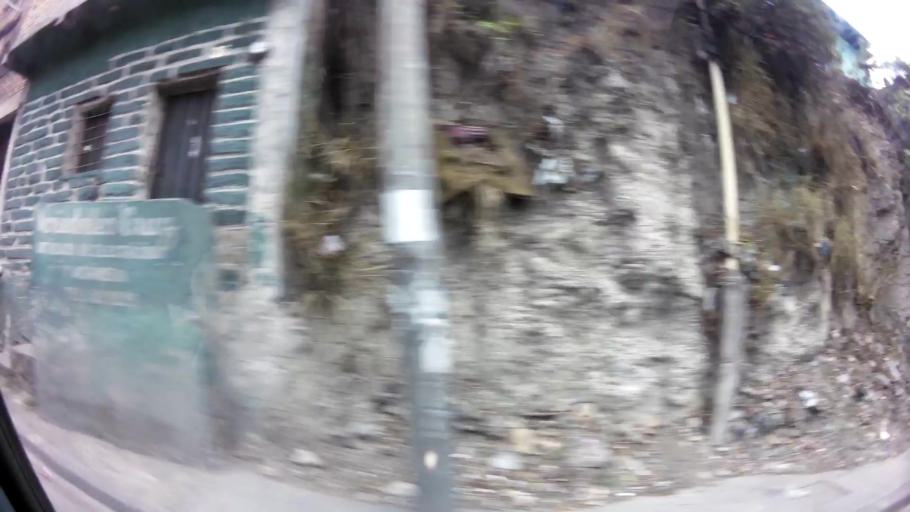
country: HN
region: Francisco Morazan
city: Tegucigalpa
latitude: 14.0950
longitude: -87.2169
